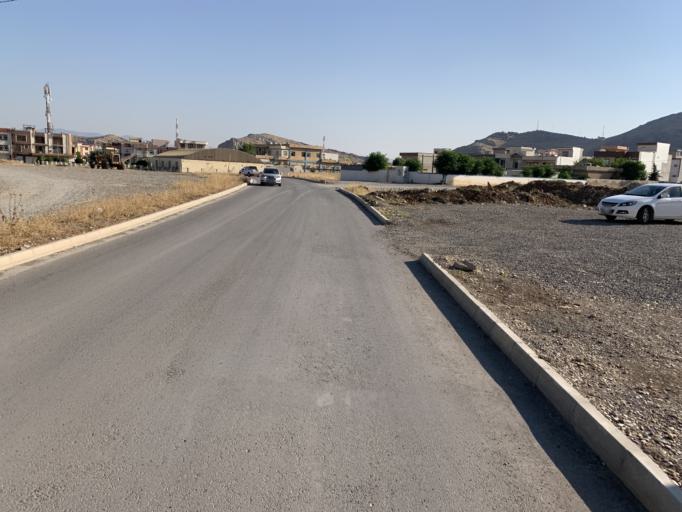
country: IQ
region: As Sulaymaniyah
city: Raniye
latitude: 36.2409
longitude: 44.8711
